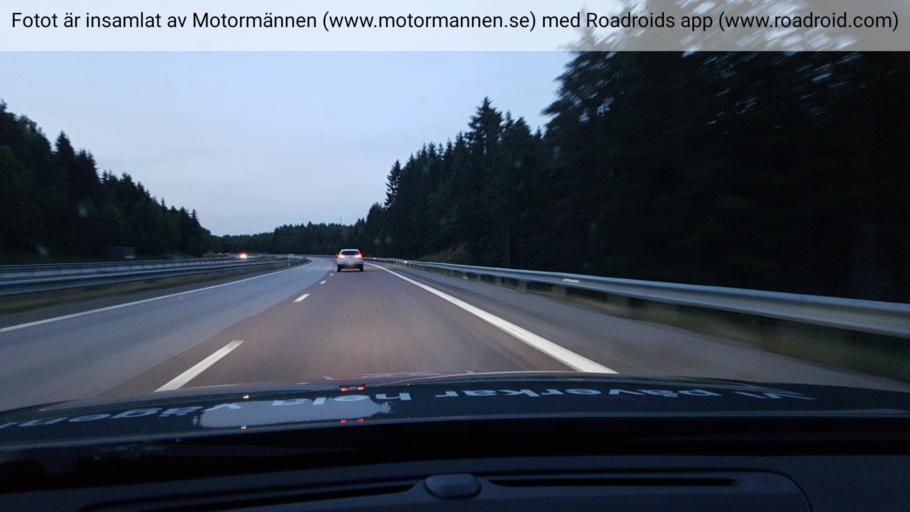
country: SE
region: Soedermanland
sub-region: Gnesta Kommun
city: Gnesta
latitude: 58.9097
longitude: 17.3351
